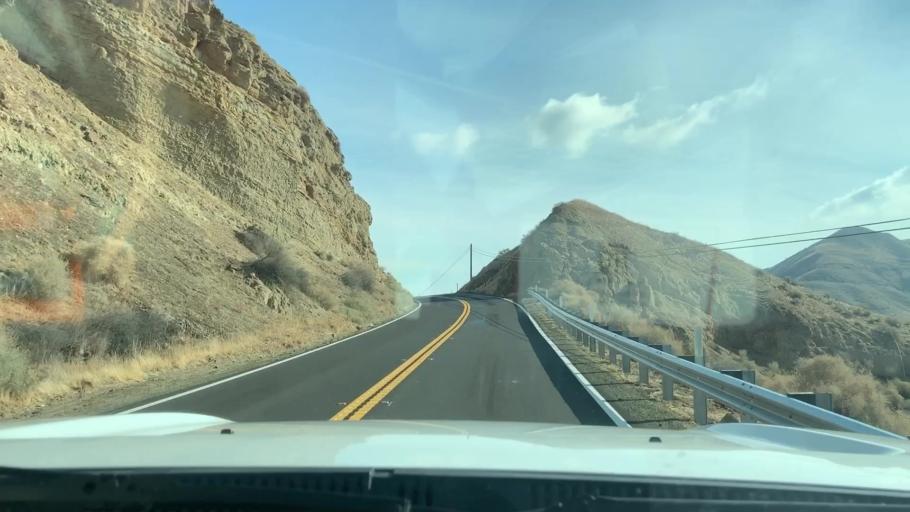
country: US
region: California
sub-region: Fresno County
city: Coalinga
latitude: 36.1080
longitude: -120.3965
